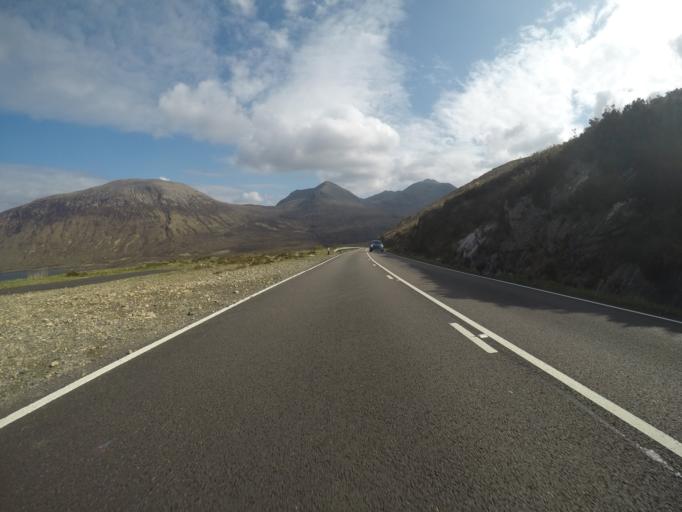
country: GB
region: Scotland
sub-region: Highland
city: Portree
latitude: 57.2722
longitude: -6.0900
